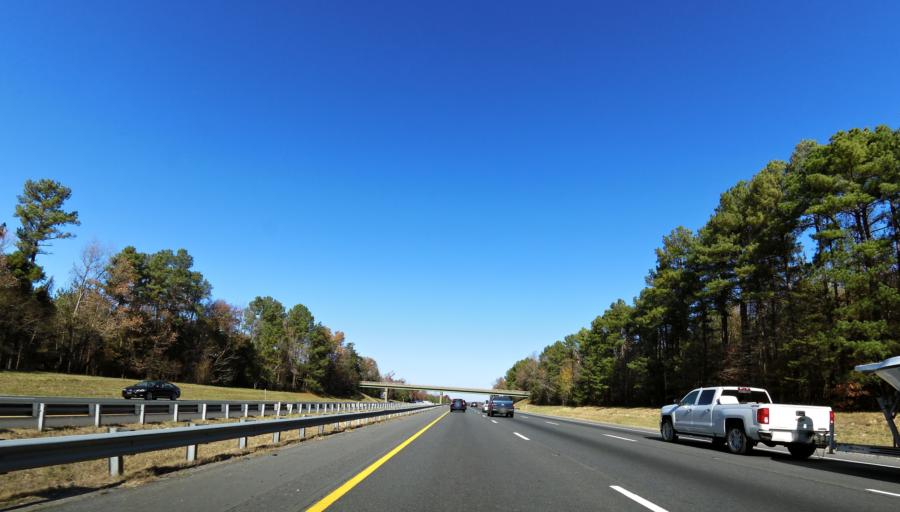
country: US
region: Virginia
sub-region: Spotsylvania County
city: Spotsylvania Courthouse
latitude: 38.1537
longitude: -77.5066
